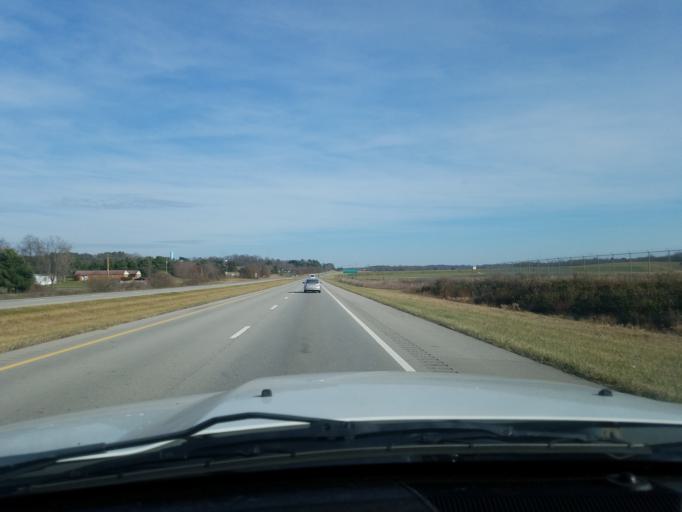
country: US
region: Ohio
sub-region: Athens County
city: Athens
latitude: 39.2167
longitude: -82.2216
